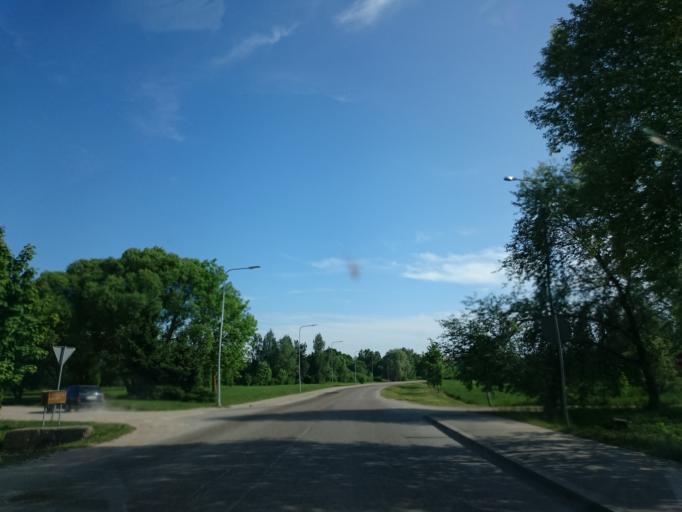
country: LV
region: Dobeles Rajons
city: Dobele
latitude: 56.6246
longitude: 23.2881
